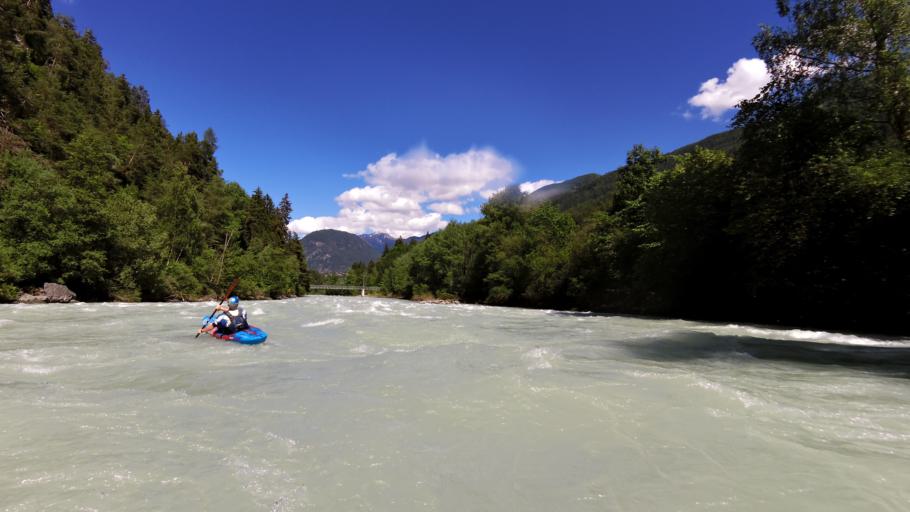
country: AT
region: Tyrol
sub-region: Politischer Bezirk Imst
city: Karres
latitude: 47.2107
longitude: 10.7958
